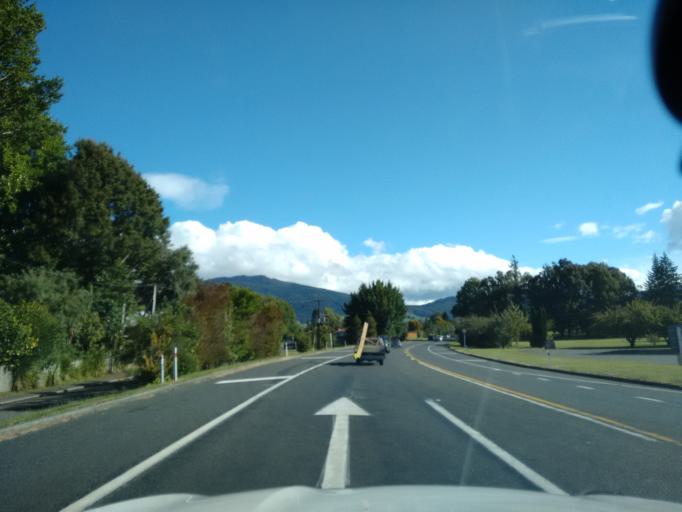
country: NZ
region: Waikato
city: Turangi
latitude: -38.9873
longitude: 175.8178
